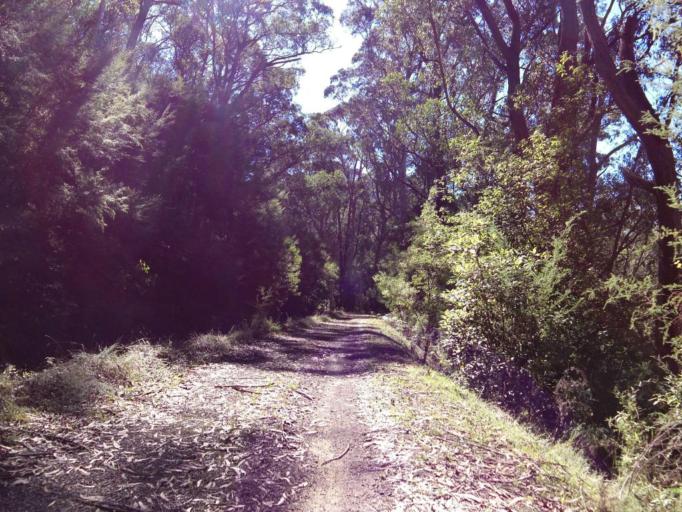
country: AU
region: Victoria
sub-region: Yarra Ranges
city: Launching Place
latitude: -37.7415
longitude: 145.5616
